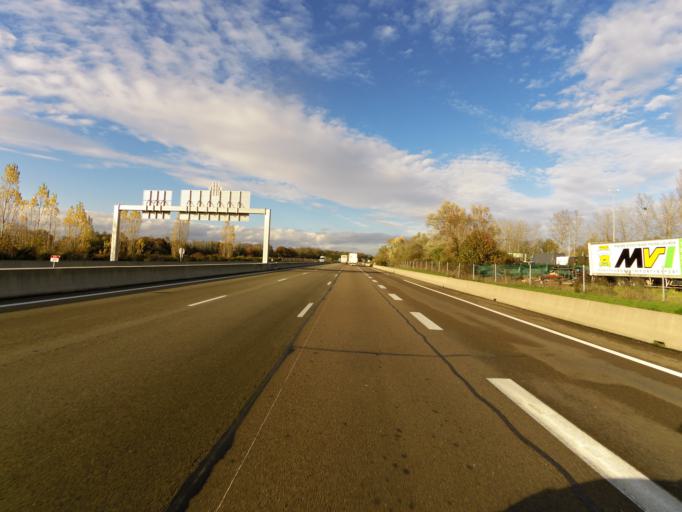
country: FR
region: Bourgogne
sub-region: Departement de la Cote-d'Or
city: Couternon
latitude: 47.3495
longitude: 5.1633
